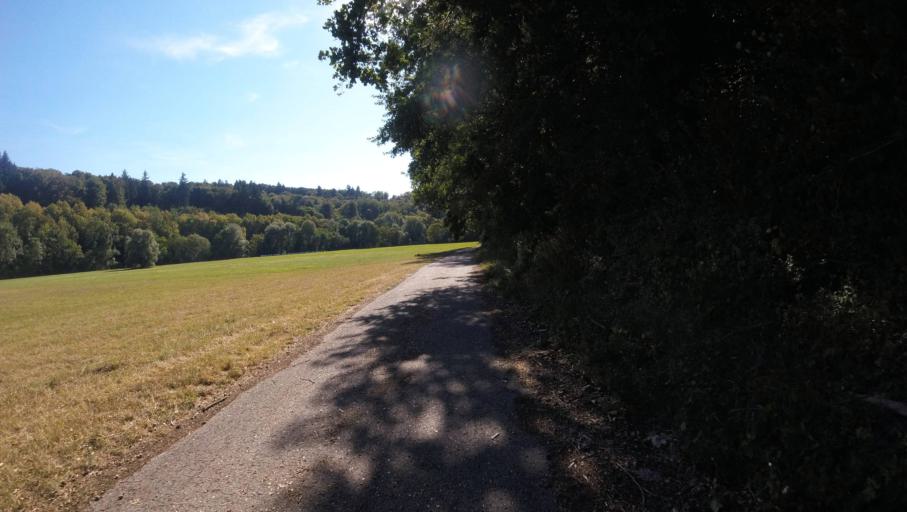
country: DE
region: Baden-Wuerttemberg
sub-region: Regierungsbezirk Stuttgart
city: Kirchberg an der Murr
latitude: 48.9318
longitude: 9.3440
